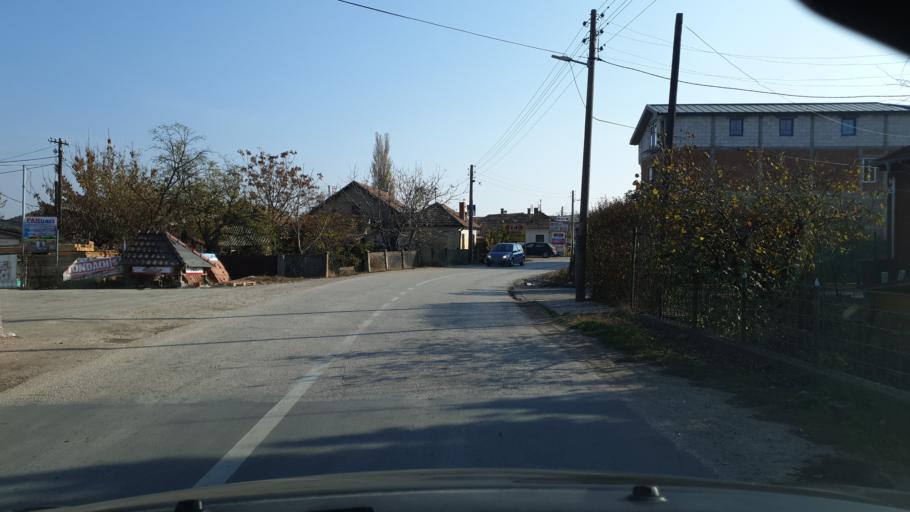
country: RS
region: Central Serbia
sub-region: Borski Okrug
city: Negotin
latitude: 44.2276
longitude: 22.5414
